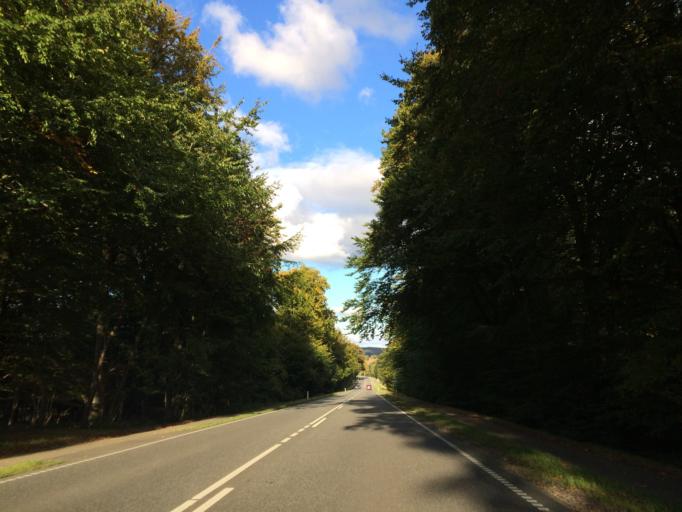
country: DK
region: Central Jutland
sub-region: Skanderborg Kommune
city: Ry
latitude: 56.0857
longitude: 9.7452
